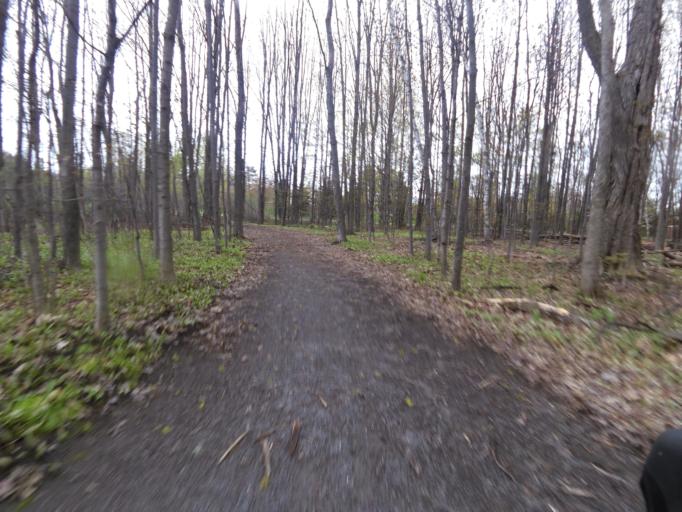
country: CA
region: Ontario
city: Bells Corners
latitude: 45.3244
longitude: -75.7685
